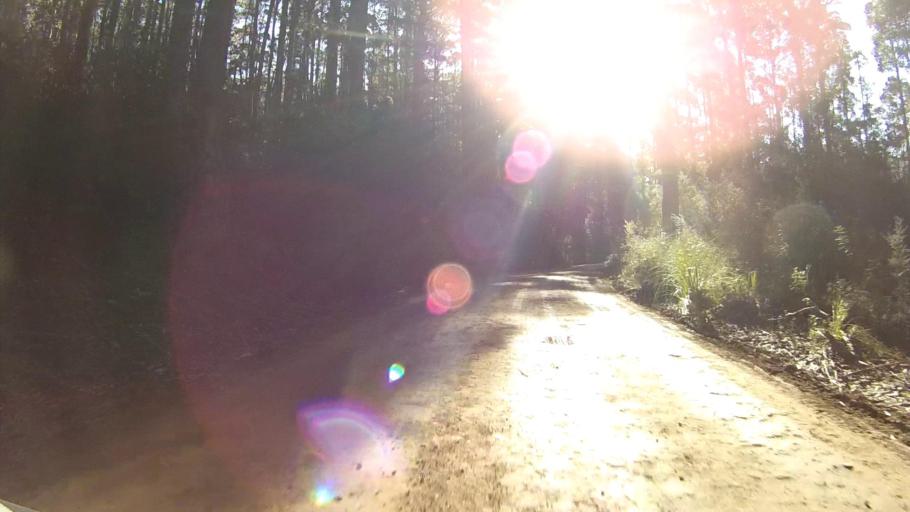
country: AU
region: Tasmania
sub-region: Clarence
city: Sandford
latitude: -43.1234
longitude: 147.9267
